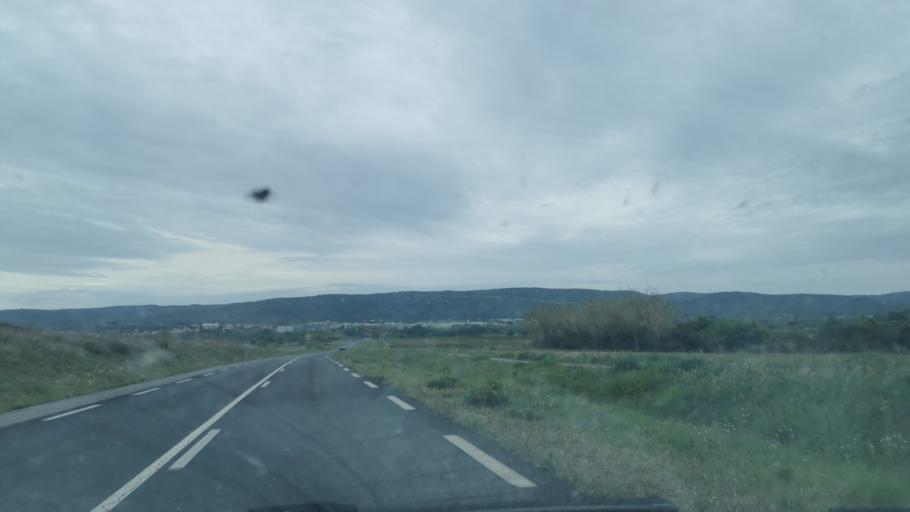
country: FR
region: Languedoc-Roussillon
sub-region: Departement de l'Herault
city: Poussan
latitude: 43.4986
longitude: 3.6861
